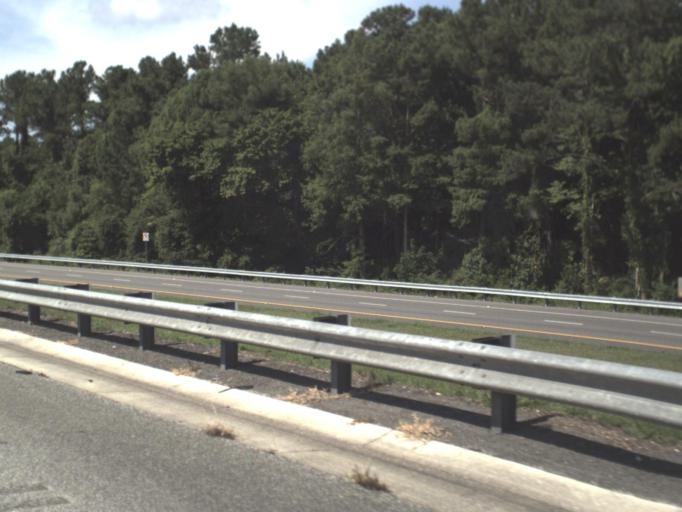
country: US
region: Florida
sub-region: Saint Johns County
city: Fruit Cove
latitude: 30.0635
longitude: -81.4982
